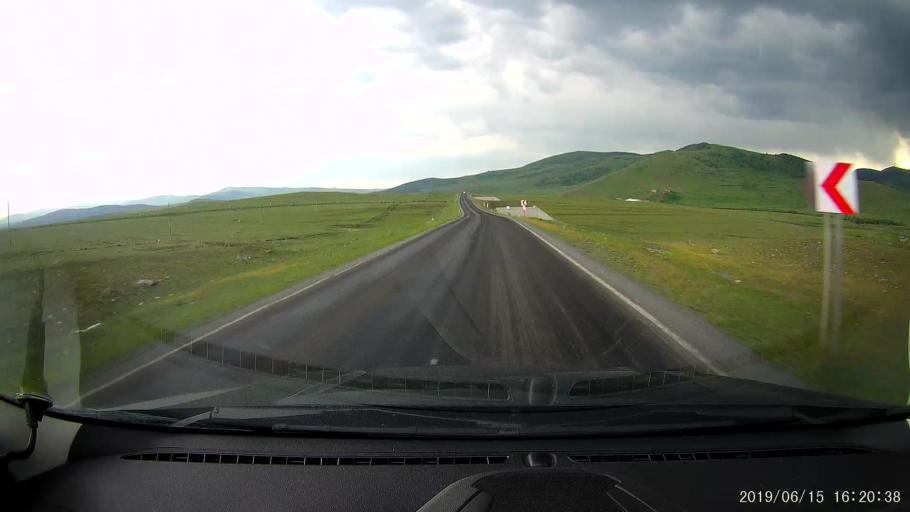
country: TR
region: Ardahan
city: Hanak
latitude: 41.2108
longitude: 42.8468
